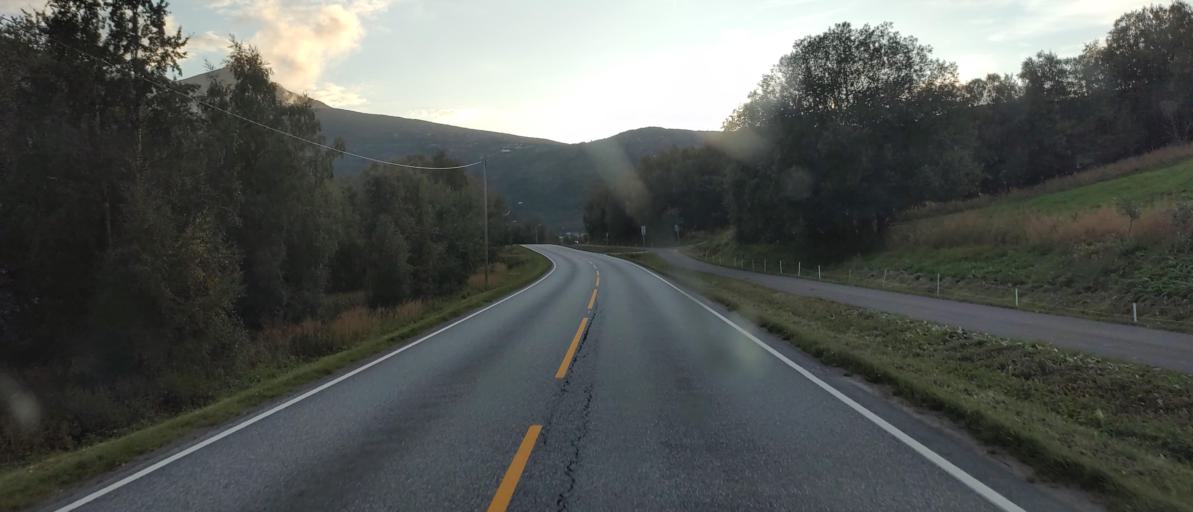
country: NO
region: Nordland
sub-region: Lodingen
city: Lodingen
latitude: 68.1935
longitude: 16.0473
